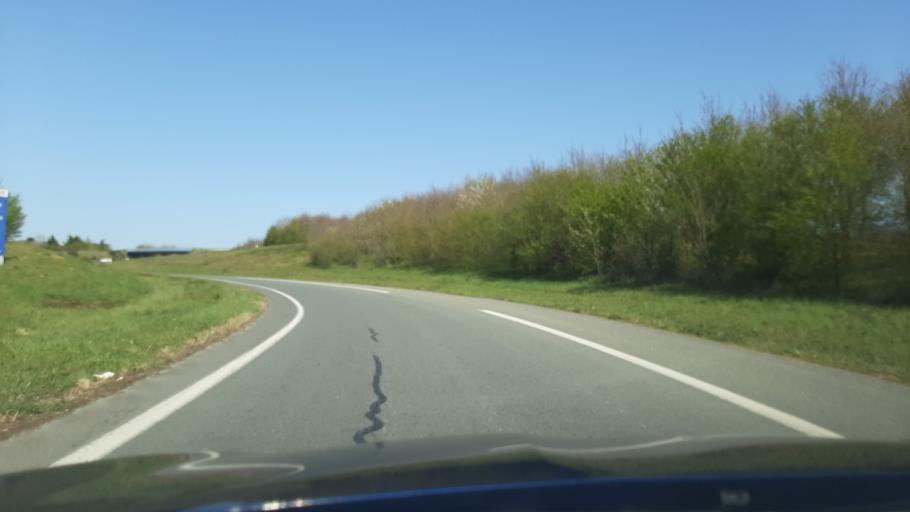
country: FR
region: Pays de la Loire
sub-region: Departement de Maine-et-Loire
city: Murs-Erigne
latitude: 47.3917
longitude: -0.5405
